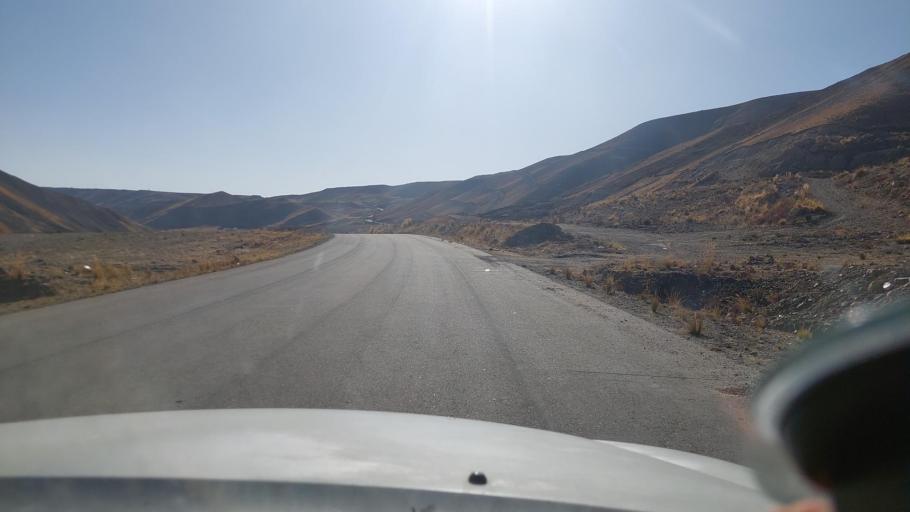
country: BO
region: La Paz
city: La Paz
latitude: -16.4217
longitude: -68.1163
